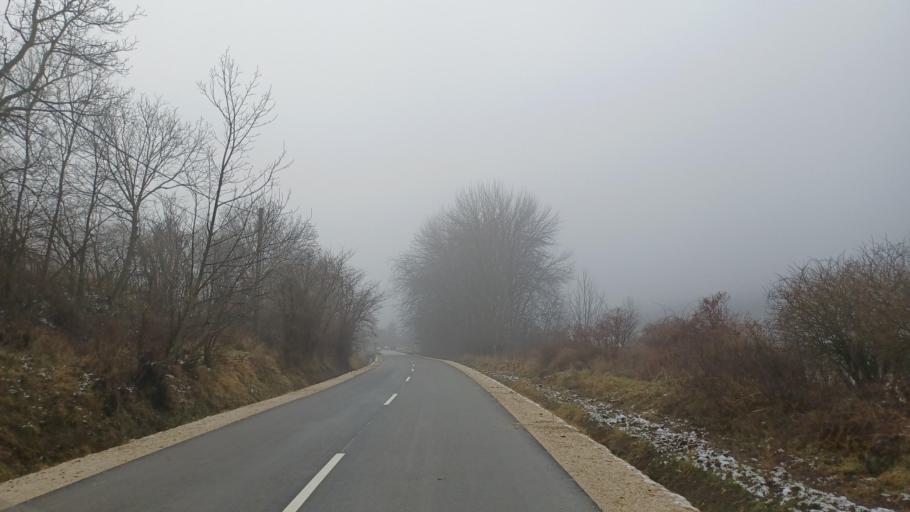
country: HU
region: Tolna
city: Gyonk
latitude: 46.5699
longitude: 18.4745
